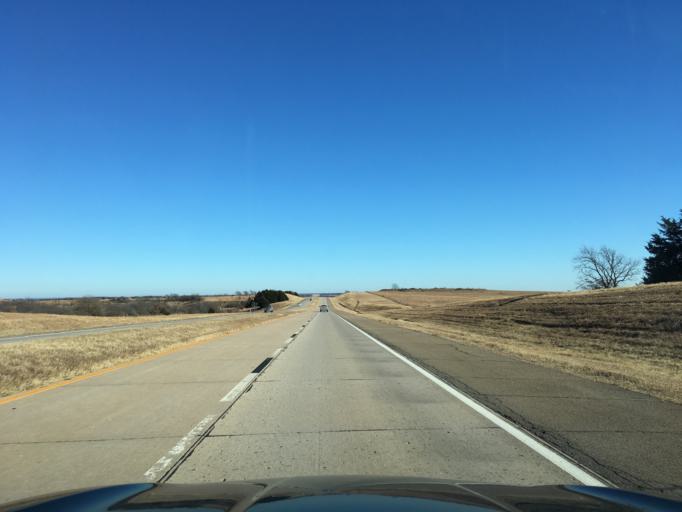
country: US
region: Oklahoma
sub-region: Payne County
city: Yale
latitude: 36.2240
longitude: -96.7405
